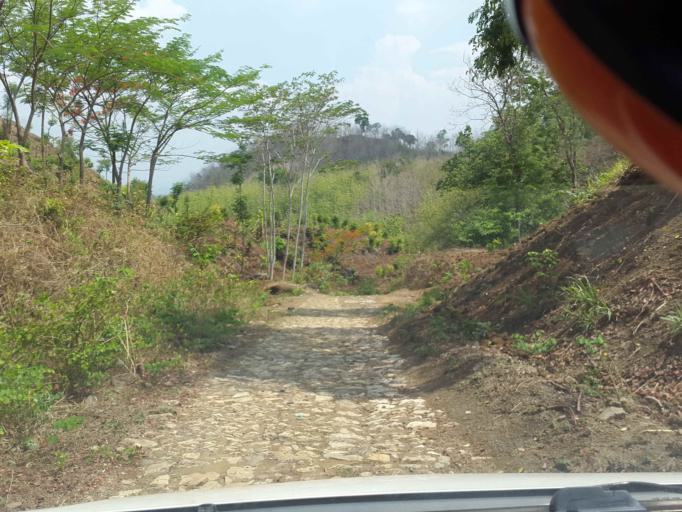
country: ID
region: East Java
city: Ponorogo
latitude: -7.8222
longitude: 111.3220
